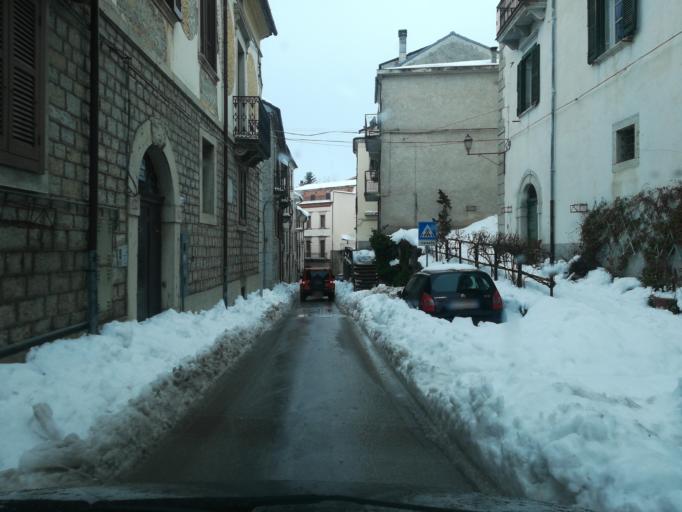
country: IT
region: Molise
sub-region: Provincia di Isernia
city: Agnone
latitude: 41.8072
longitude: 14.3677
